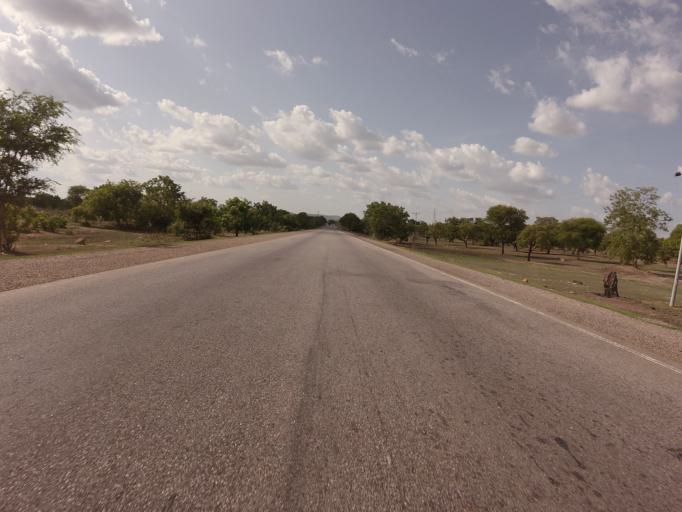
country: GH
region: Upper East
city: Bolgatanga
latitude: 10.5748
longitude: -0.8327
